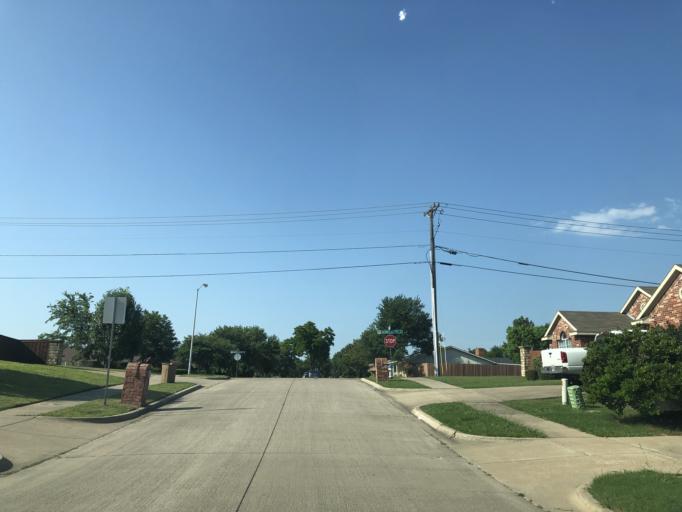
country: US
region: Texas
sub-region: Dallas County
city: Sunnyvale
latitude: 32.8250
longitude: -96.5993
